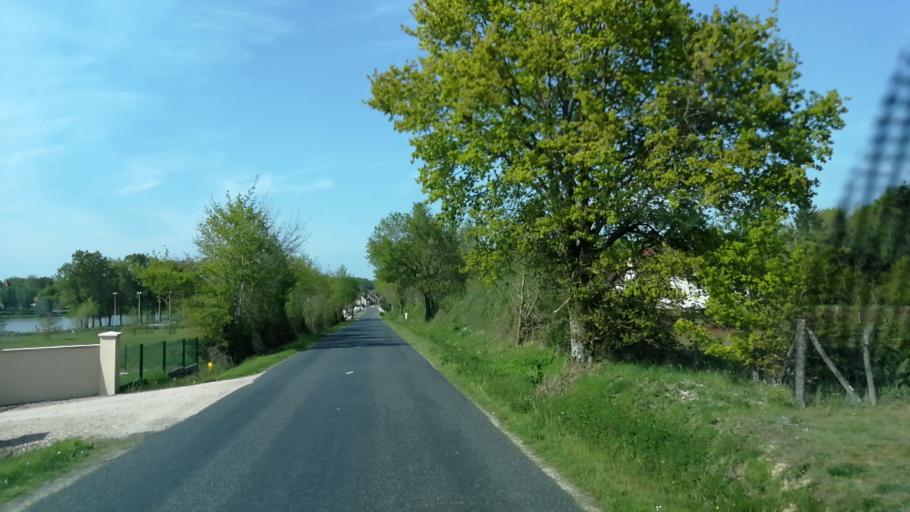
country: FR
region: Auvergne
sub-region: Departement de l'Allier
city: Neuilly-le-Real
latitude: 46.4846
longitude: 3.5227
